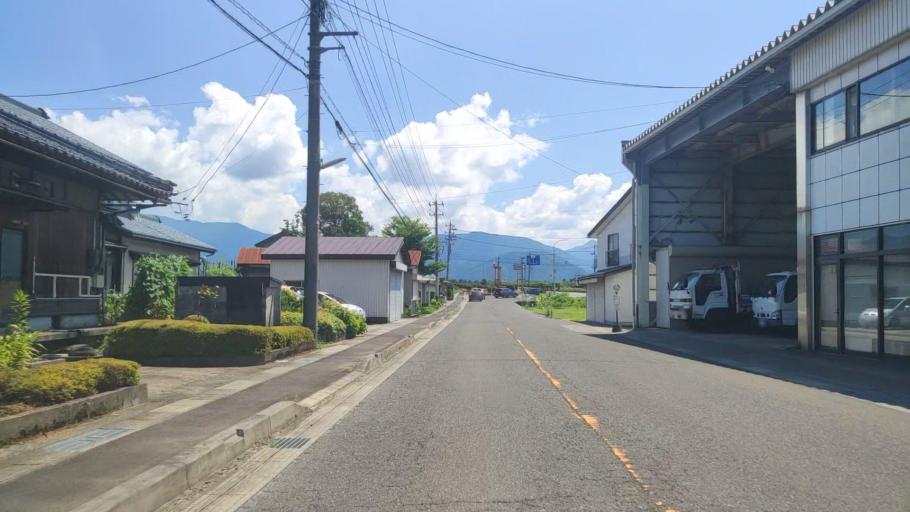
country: JP
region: Fukui
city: Ono
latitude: 35.9793
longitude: 136.5181
